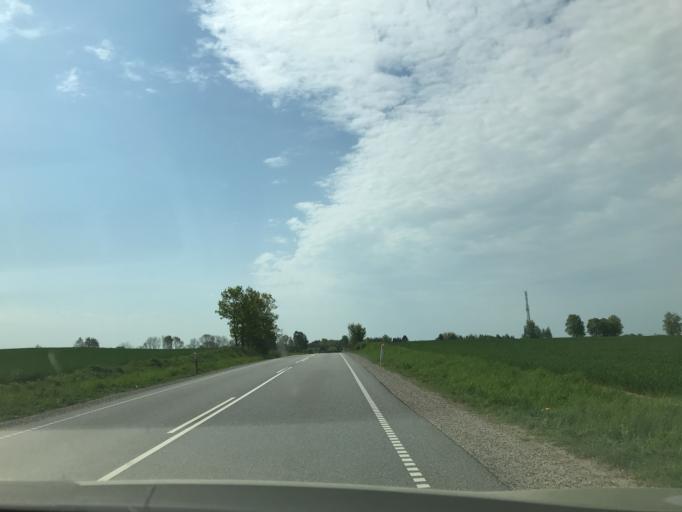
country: DK
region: South Denmark
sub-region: Middelfart Kommune
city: Ejby
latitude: 55.3812
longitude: 9.9176
